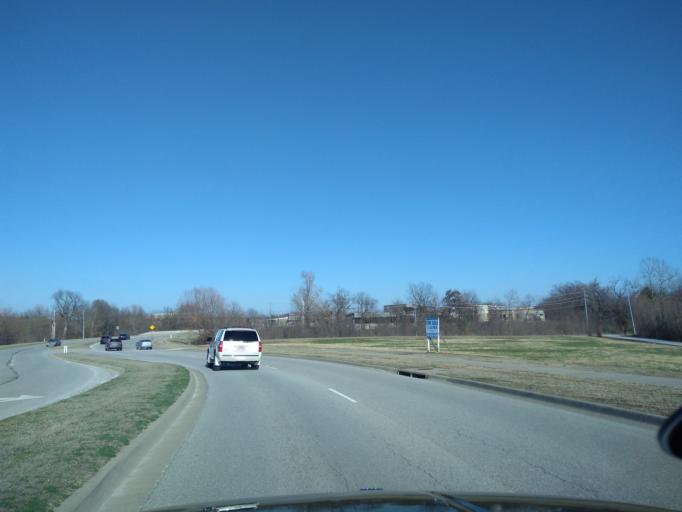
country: US
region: Arkansas
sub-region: Washington County
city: Johnson
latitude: 36.1170
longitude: -94.1627
